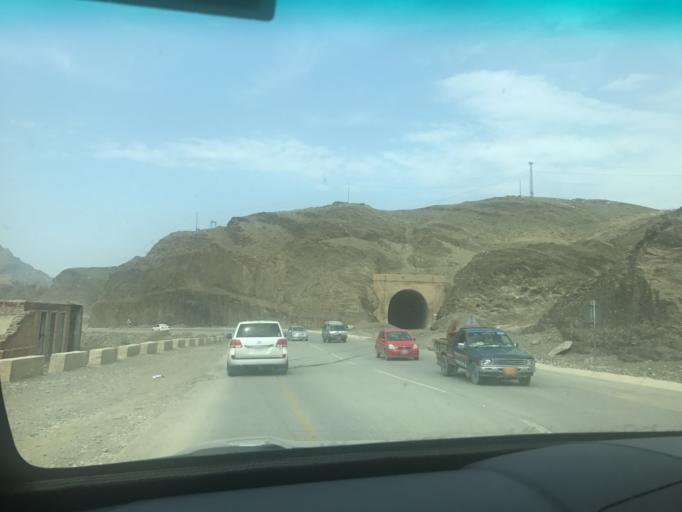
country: PK
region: Federally Administered Tribal Areas
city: Landi Kotal
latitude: 34.1015
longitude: 71.1366
